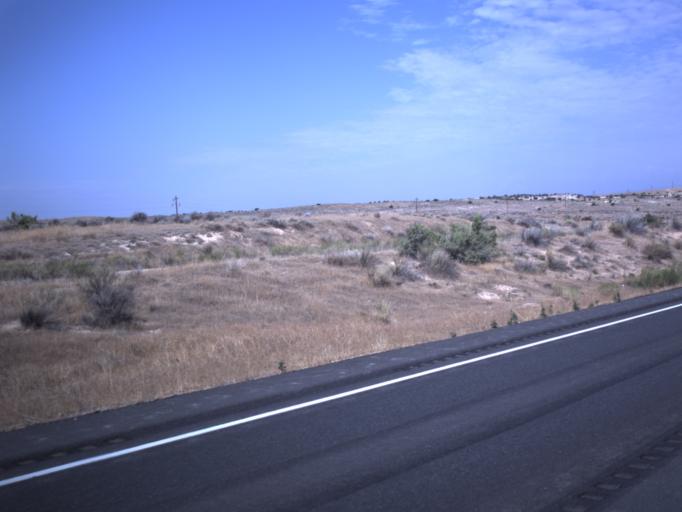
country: US
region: Utah
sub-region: Uintah County
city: Naples
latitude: 40.3419
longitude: -109.2978
